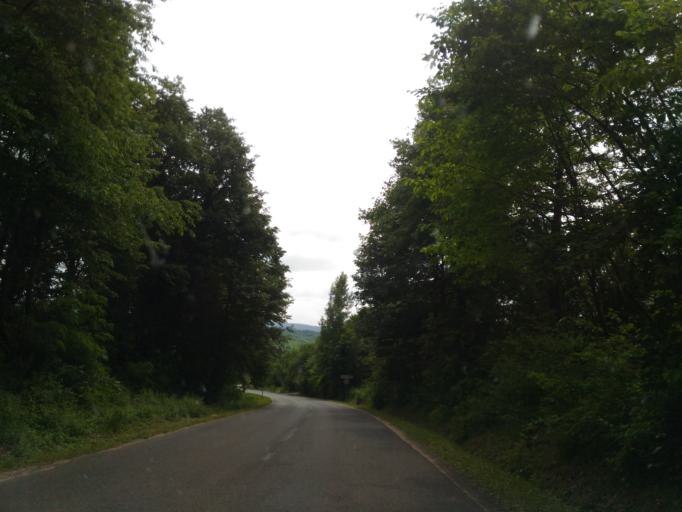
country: HU
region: Baranya
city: Komlo
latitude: 46.1813
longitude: 18.2322
